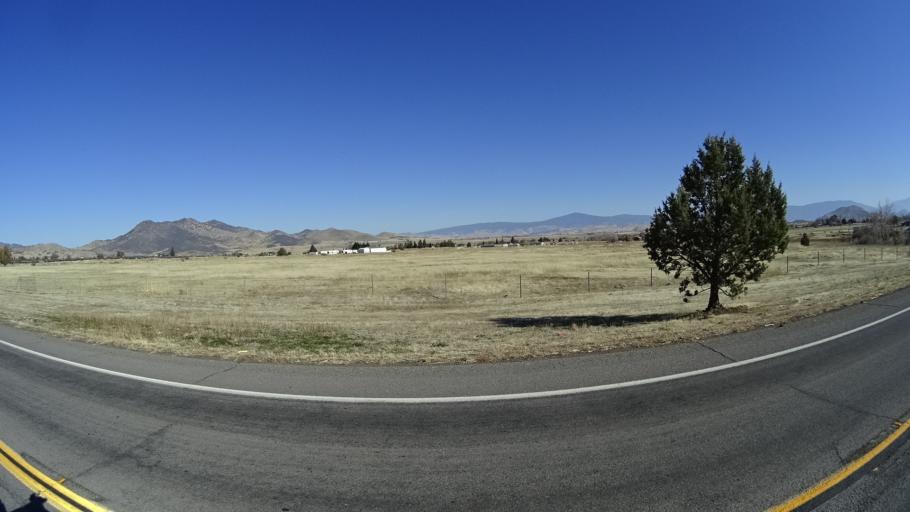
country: US
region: California
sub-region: Siskiyou County
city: Yreka
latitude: 41.7393
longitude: -122.5971
